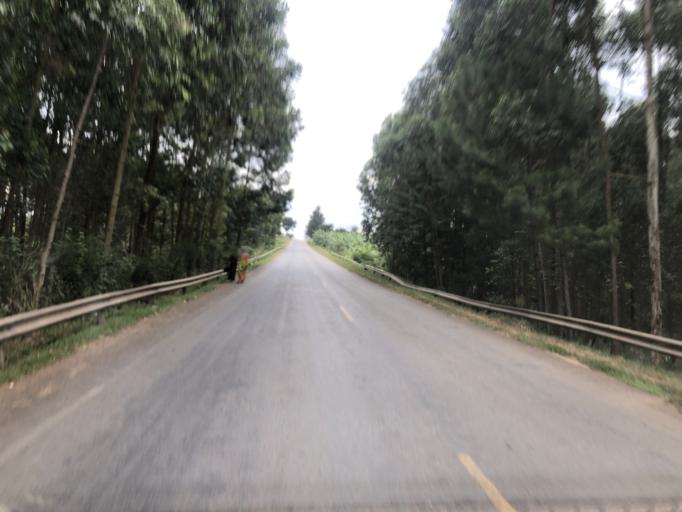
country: UG
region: Western Region
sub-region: Sheema District
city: Kibingo
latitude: -0.5790
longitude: 30.4119
